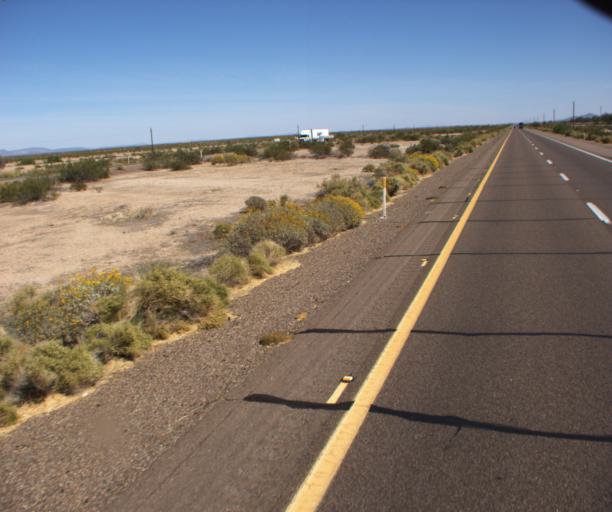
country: US
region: Arizona
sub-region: Yuma County
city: Wellton
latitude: 32.7374
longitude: -113.6960
